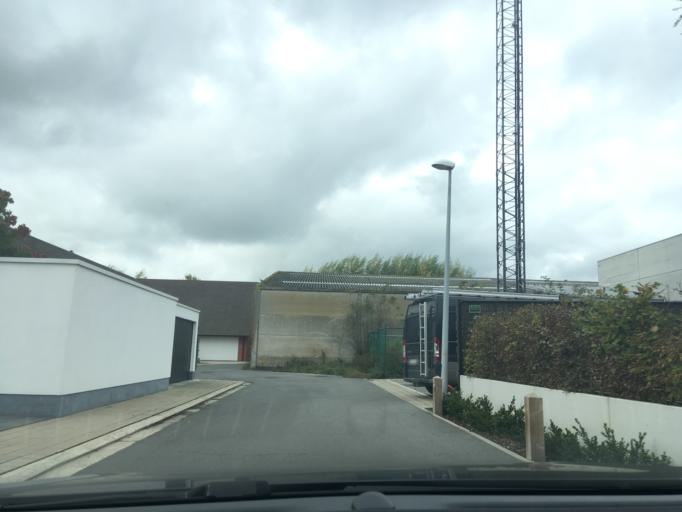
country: BE
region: Flanders
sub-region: Provincie West-Vlaanderen
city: Moorslede
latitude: 50.8913
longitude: 3.0516
